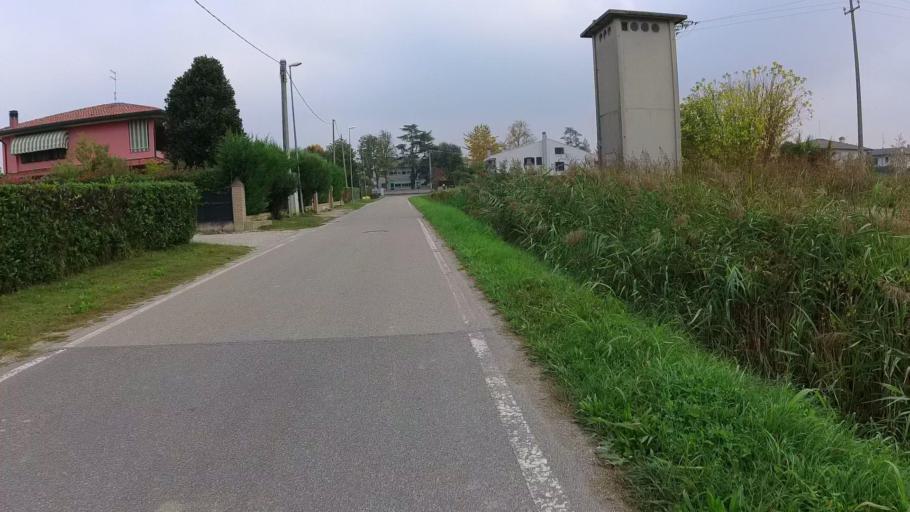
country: IT
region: Veneto
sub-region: Provincia di Venezia
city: Fosso
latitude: 45.3875
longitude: 12.0402
